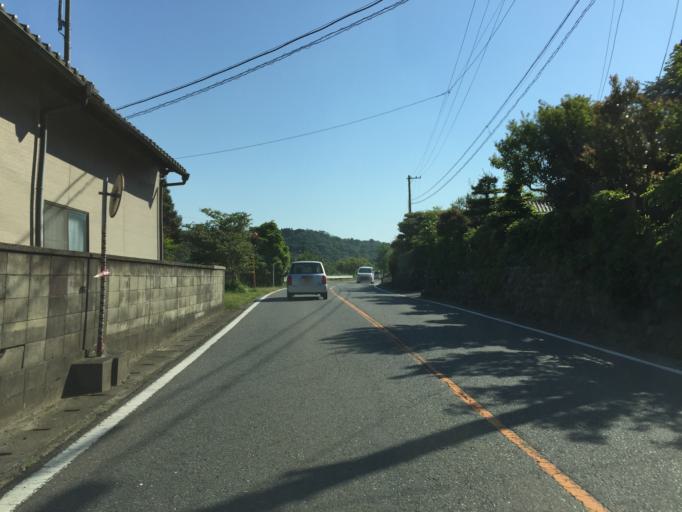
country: JP
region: Fukushima
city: Iwaki
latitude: 36.9432
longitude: 140.8199
